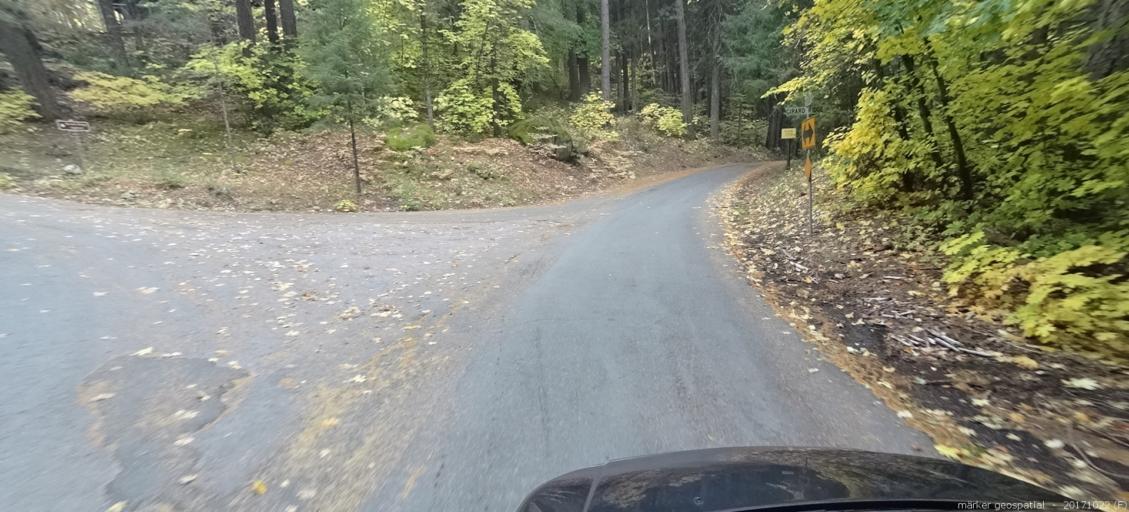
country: US
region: California
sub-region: Siskiyou County
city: Dunsmuir
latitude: 41.1523
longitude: -122.2893
